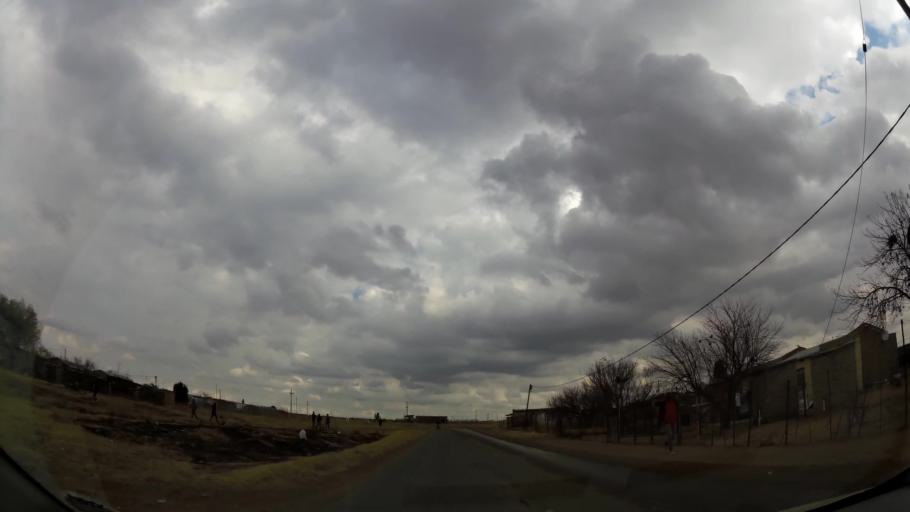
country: ZA
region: Orange Free State
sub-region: Fezile Dabi District Municipality
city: Sasolburg
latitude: -26.8563
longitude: 27.8724
